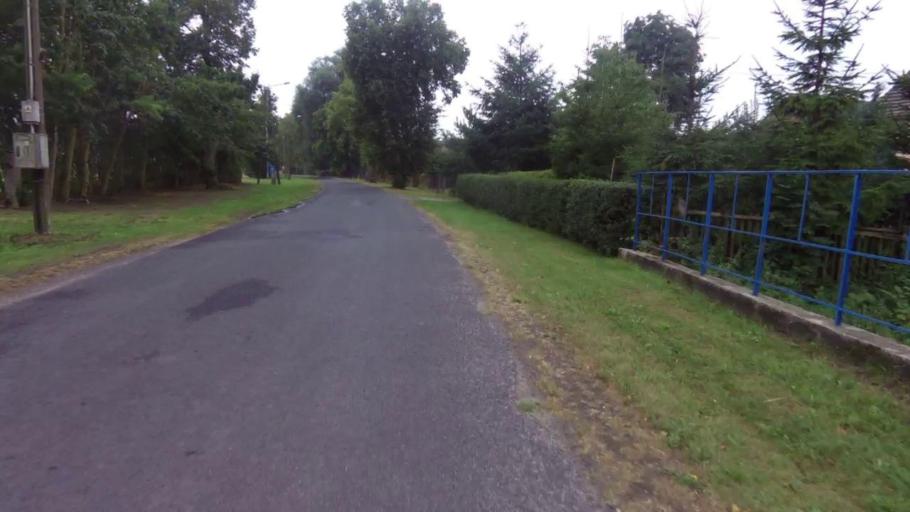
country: PL
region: West Pomeranian Voivodeship
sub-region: Powiat choszczenski
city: Choszczno
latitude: 53.2261
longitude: 15.3800
